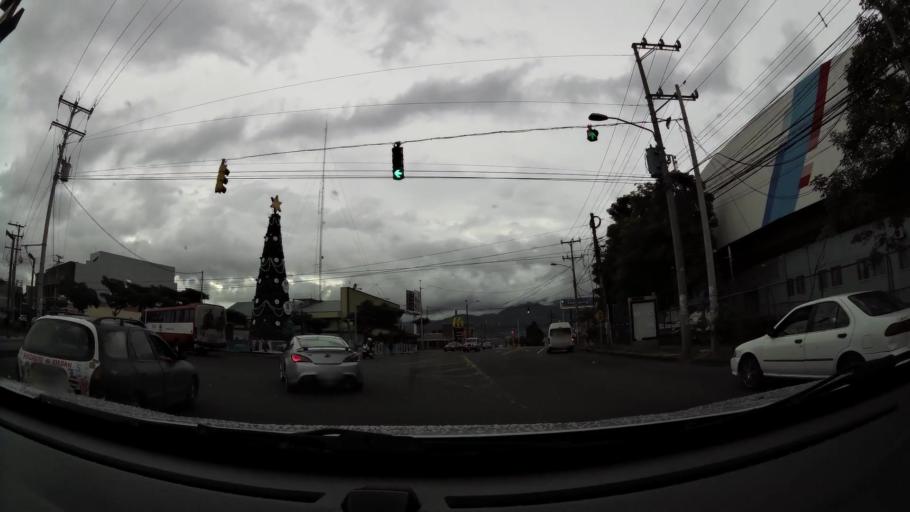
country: CR
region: San Jose
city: San Jose
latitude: 9.9333
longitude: -84.0982
